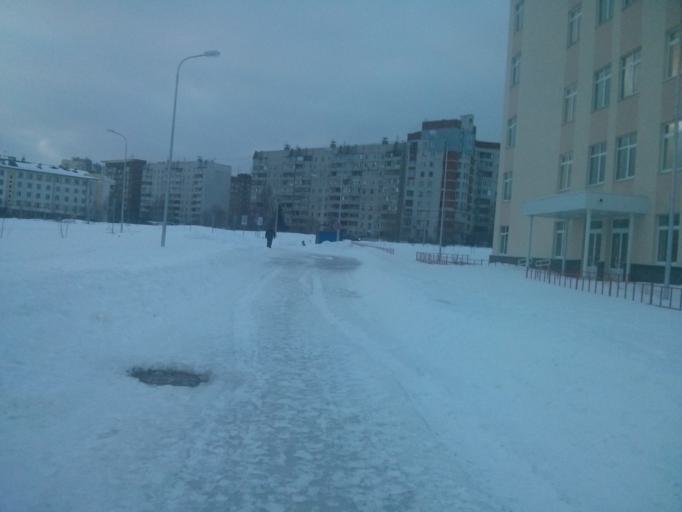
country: RU
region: Nizjnij Novgorod
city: Afonino
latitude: 56.2854
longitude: 44.0842
